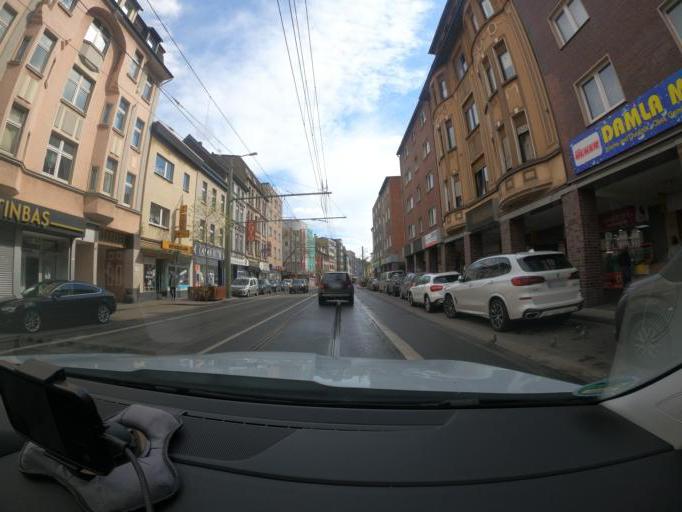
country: DE
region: North Rhine-Westphalia
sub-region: Regierungsbezirk Dusseldorf
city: Hochfeld
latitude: 51.4204
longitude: 6.7543
